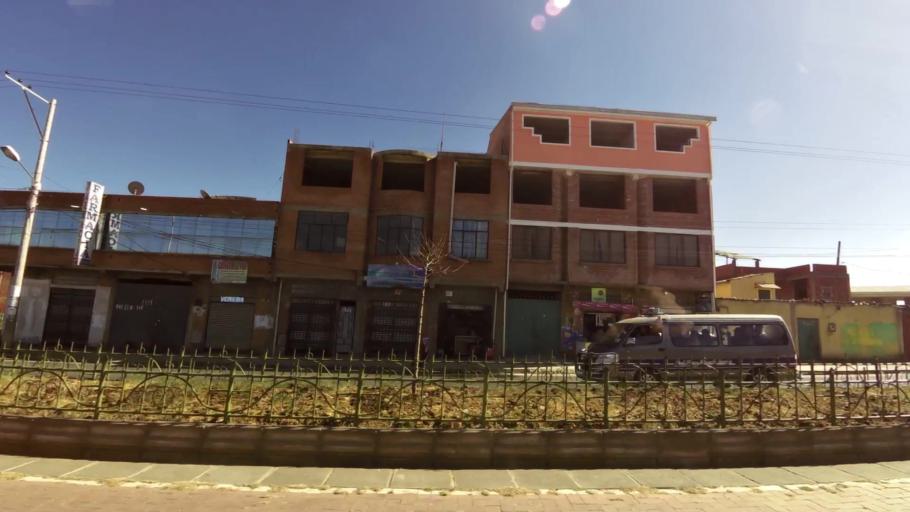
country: BO
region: La Paz
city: La Paz
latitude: -16.5184
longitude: -68.1849
